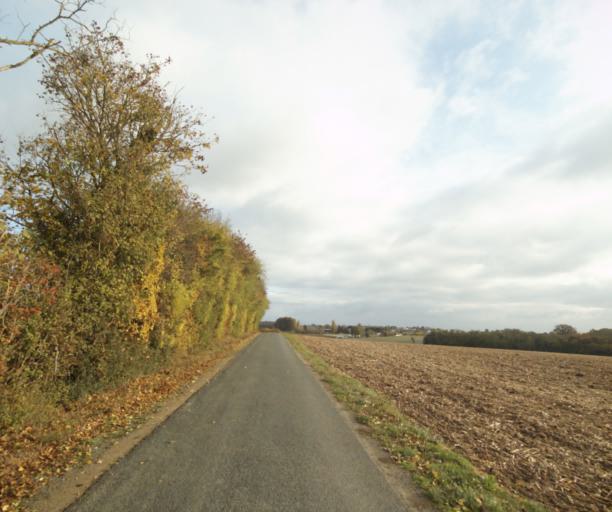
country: FR
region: Poitou-Charentes
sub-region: Departement de la Charente-Maritime
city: Saint-Georges-des-Coteaux
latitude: 45.7818
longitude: -0.7279
